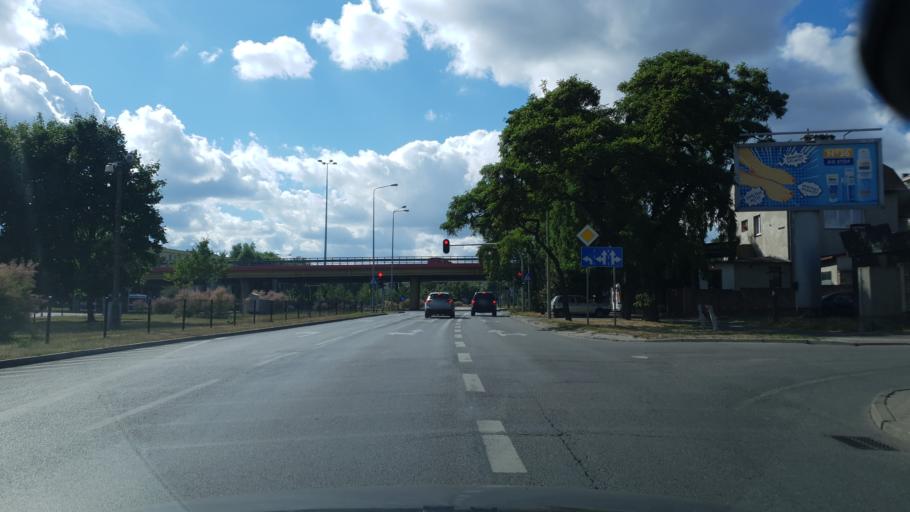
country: PL
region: Pomeranian Voivodeship
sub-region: Gdynia
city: Pogorze
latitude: 54.5510
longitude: 18.5086
